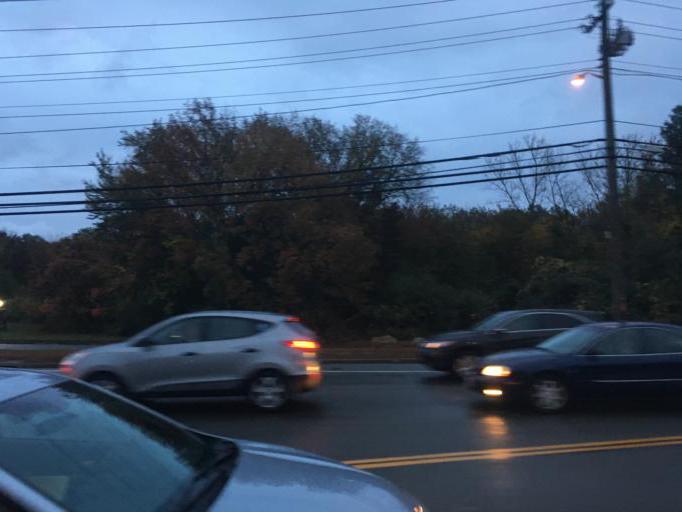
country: US
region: Rhode Island
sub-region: Kent County
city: West Warwick
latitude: 41.6707
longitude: -71.4997
